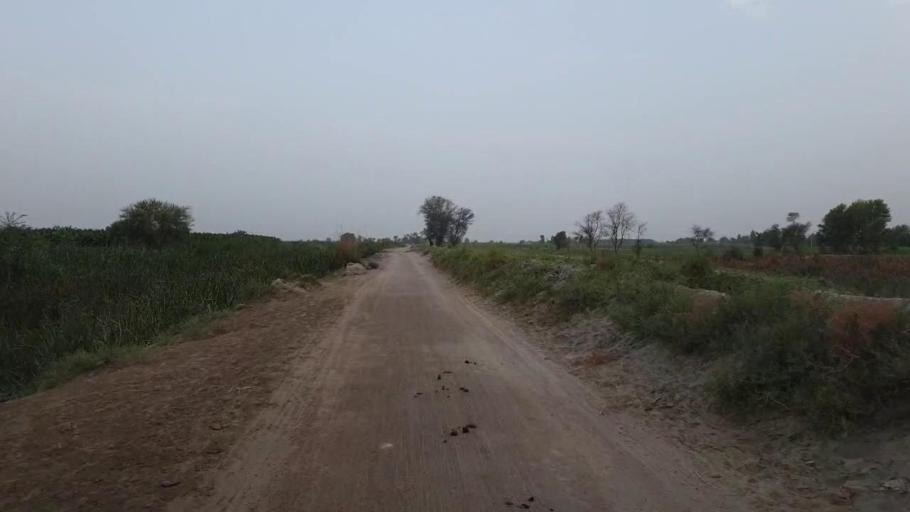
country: PK
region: Sindh
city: Daur
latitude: 26.4108
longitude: 68.2252
